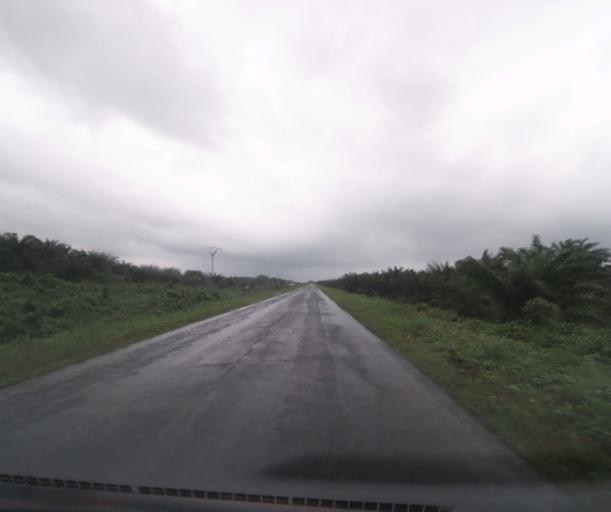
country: CM
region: South-West Province
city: Idenao
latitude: 4.1571
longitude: 8.9925
